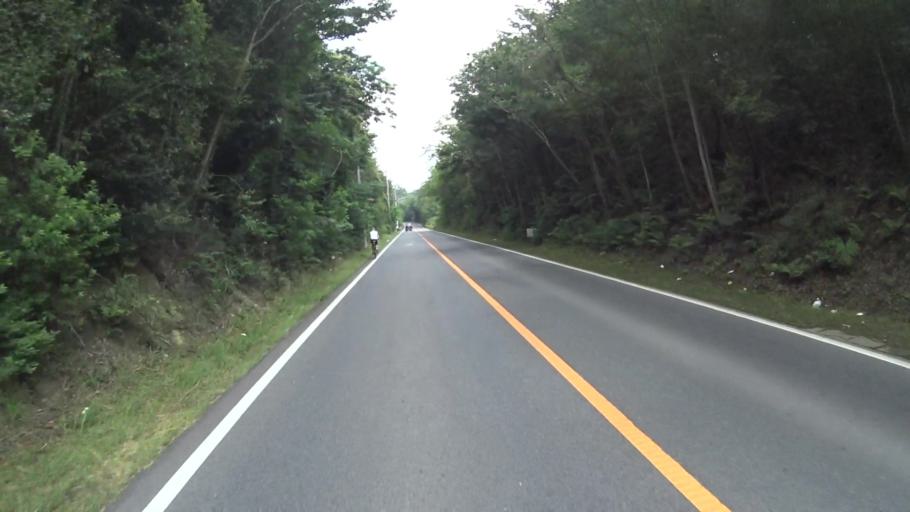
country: JP
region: Kyoto
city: Tanabe
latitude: 34.8057
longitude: 135.7421
